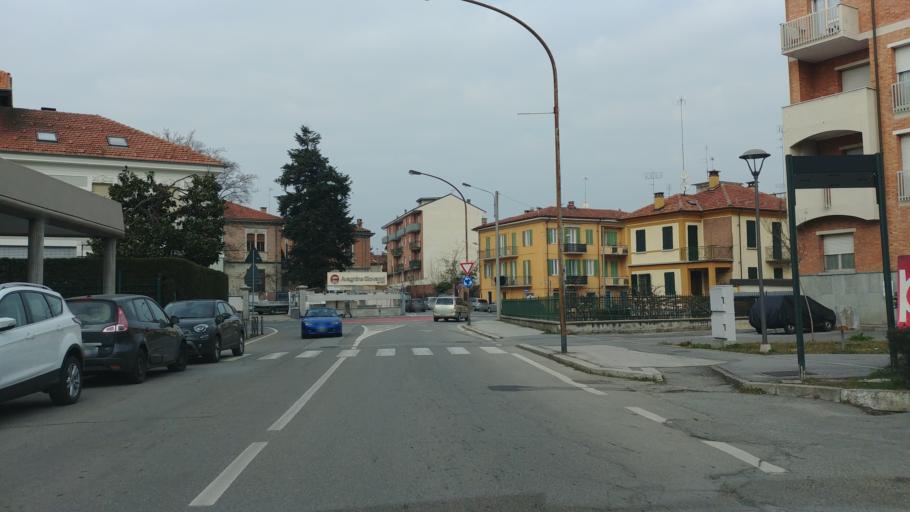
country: IT
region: Piedmont
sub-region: Provincia di Cuneo
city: Fossano
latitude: 44.5438
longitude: 7.7204
